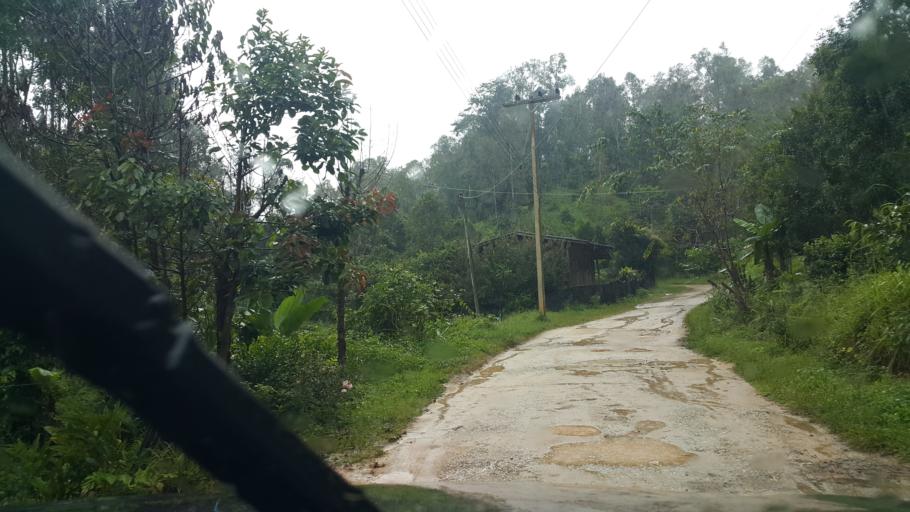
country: TH
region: Chiang Mai
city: Phrao
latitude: 19.1279
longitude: 99.3345
